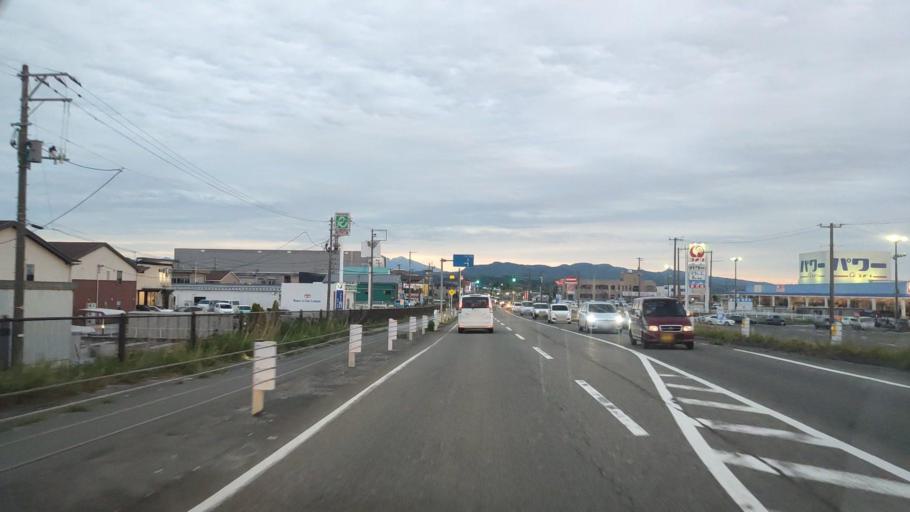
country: JP
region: Niigata
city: Niitsu-honcho
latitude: 37.7910
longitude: 139.1112
